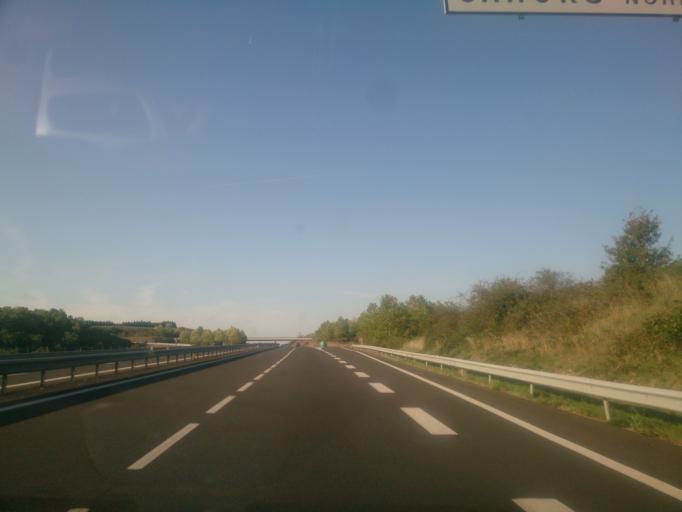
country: FR
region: Midi-Pyrenees
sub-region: Departement du Lot
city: Cahors
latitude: 44.5268
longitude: 1.5117
